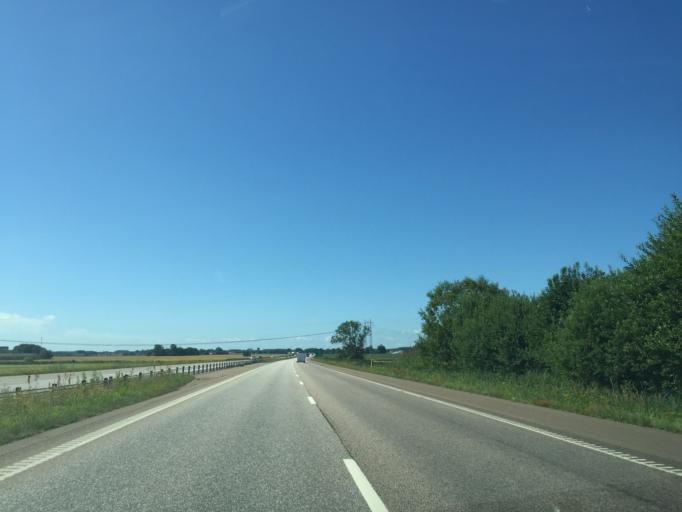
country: SE
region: Skane
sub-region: Angelholms Kommun
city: Strovelstorp
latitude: 56.1287
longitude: 12.8288
